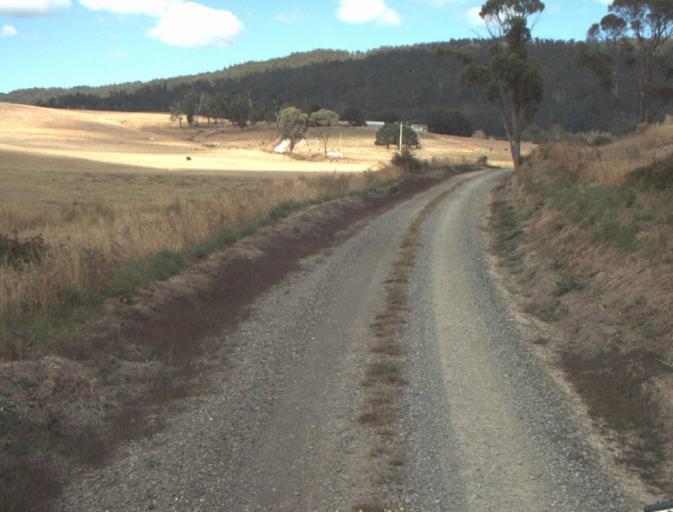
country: AU
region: Tasmania
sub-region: Launceston
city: Mayfield
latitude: -41.2101
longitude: 147.1096
